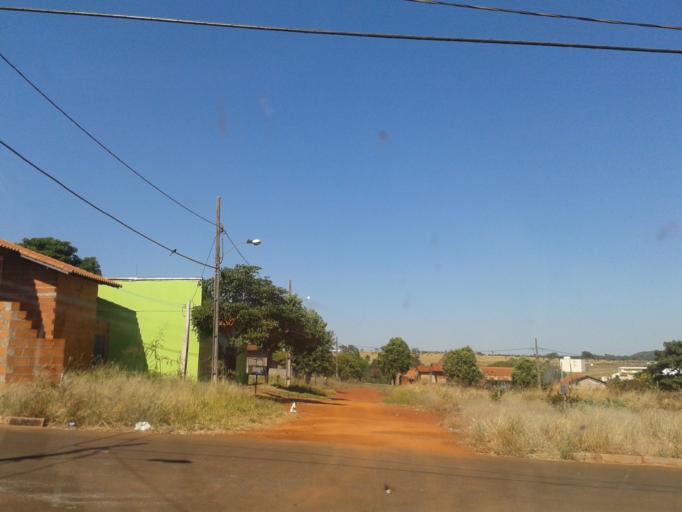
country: BR
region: Minas Gerais
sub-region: Ituiutaba
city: Ituiutaba
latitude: -18.9966
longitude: -49.4600
